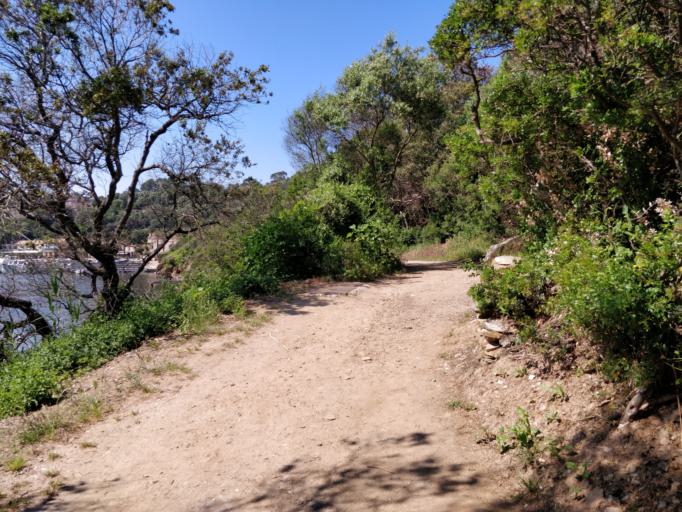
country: FR
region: Provence-Alpes-Cote d'Azur
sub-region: Departement du Var
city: Le Lavandou
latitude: 43.0080
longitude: 6.3837
